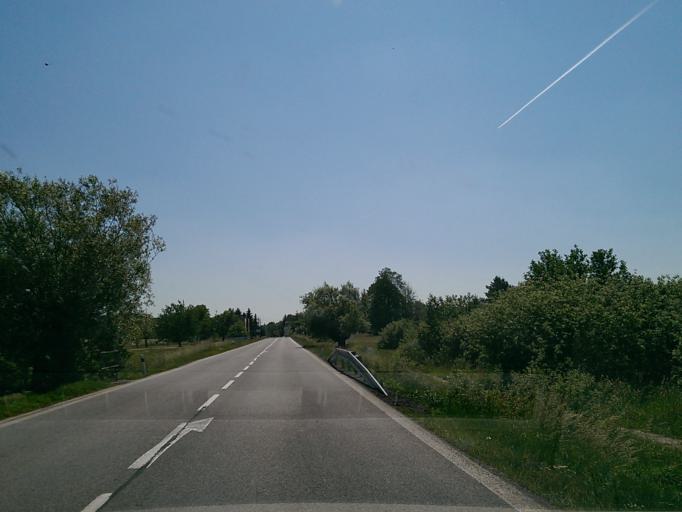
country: CZ
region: Liberecky
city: Rovensko pod Troskami
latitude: 50.5466
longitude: 15.2191
